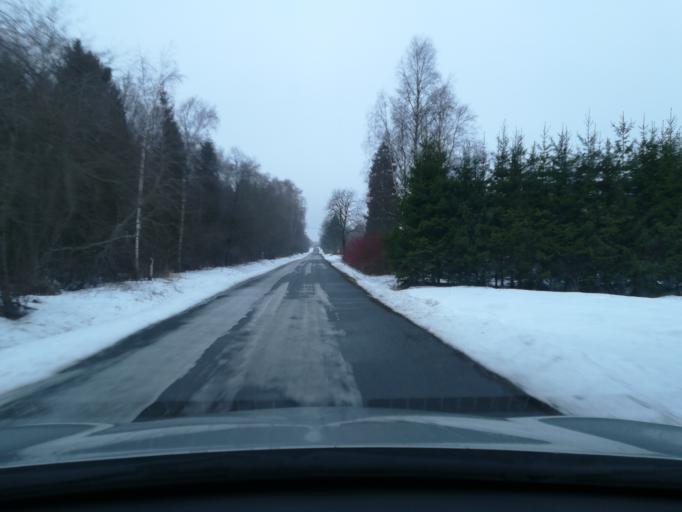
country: EE
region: Harju
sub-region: Raasiku vald
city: Raasiku
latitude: 59.3429
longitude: 25.2465
